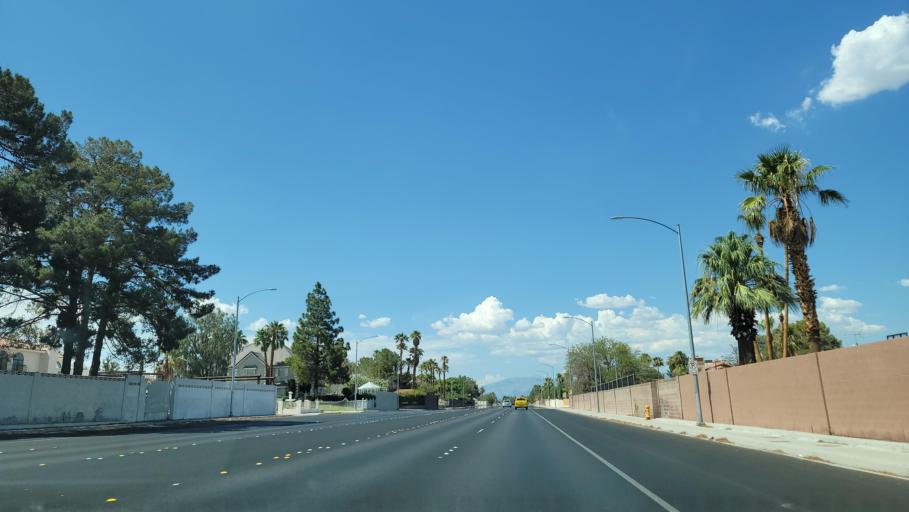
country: US
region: Nevada
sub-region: Clark County
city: Spring Valley
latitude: 36.1369
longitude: -115.2609
